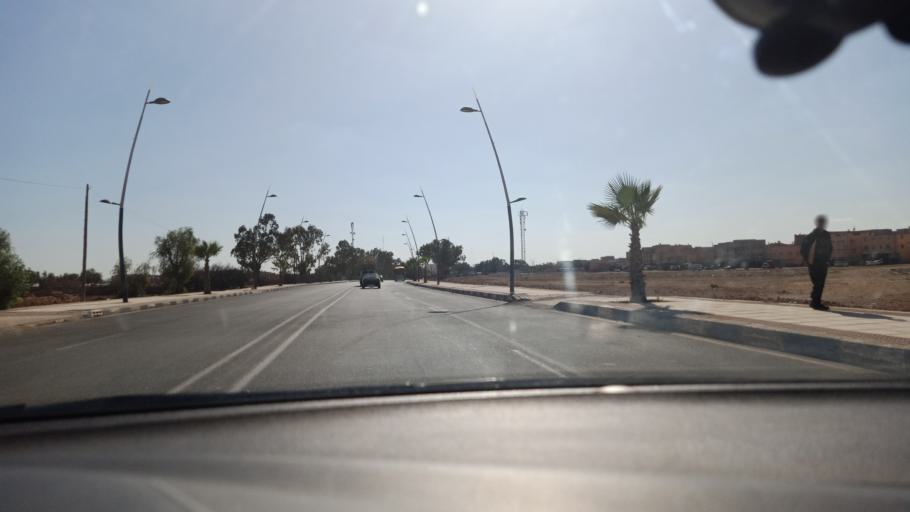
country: MA
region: Doukkala-Abda
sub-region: Safi
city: Youssoufia
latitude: 32.0850
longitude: -8.6197
